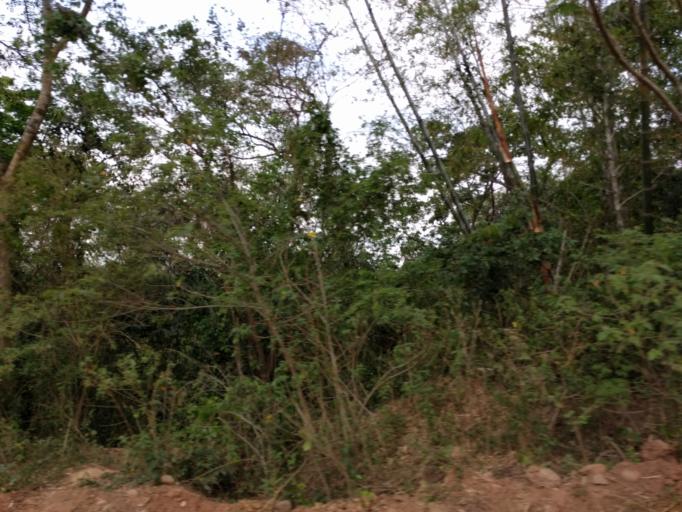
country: BO
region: Santa Cruz
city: Santa Rita
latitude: -17.9294
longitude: -63.3911
